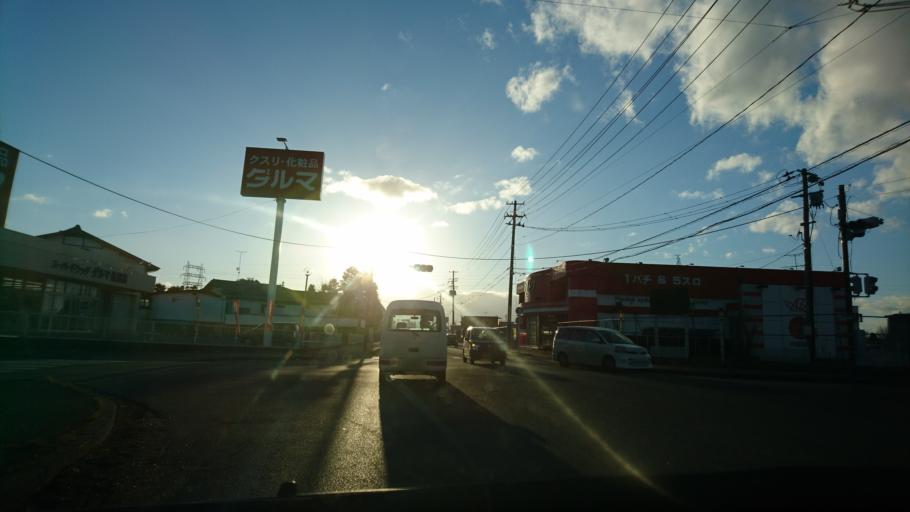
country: JP
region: Miyagi
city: Wakuya
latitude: 38.6965
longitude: 141.2089
